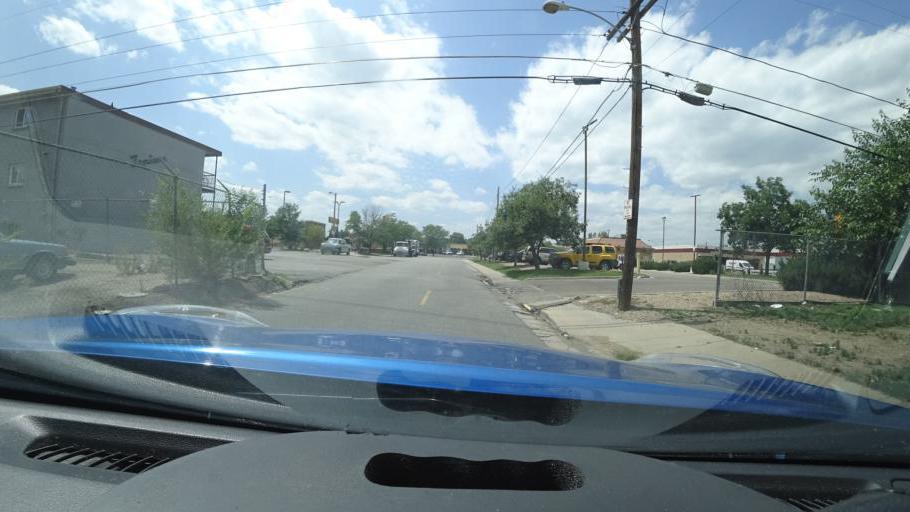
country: US
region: Colorado
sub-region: Arapahoe County
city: Sheridan
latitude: 39.6806
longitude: -105.0236
